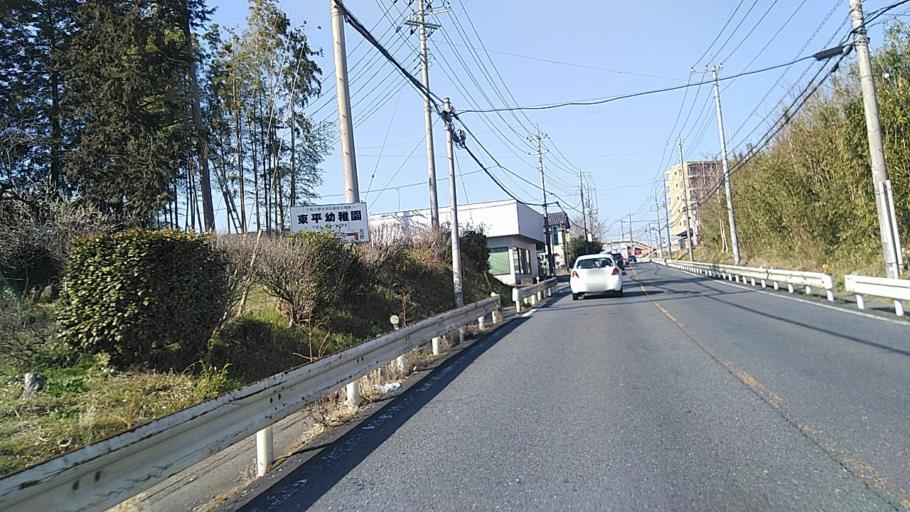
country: JP
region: Saitama
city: Fukiage-fujimi
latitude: 36.0635
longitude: 139.4082
